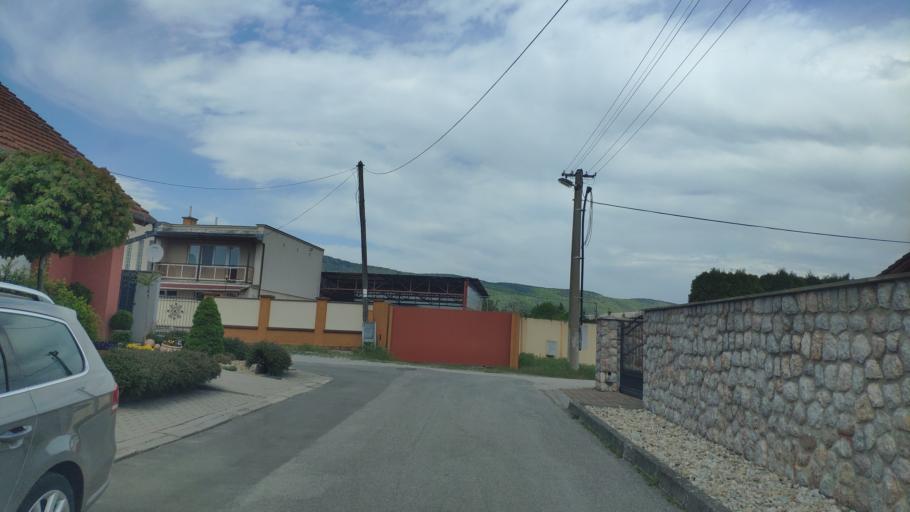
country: SK
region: Kosicky
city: Medzev
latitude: 48.6063
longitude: 20.8791
